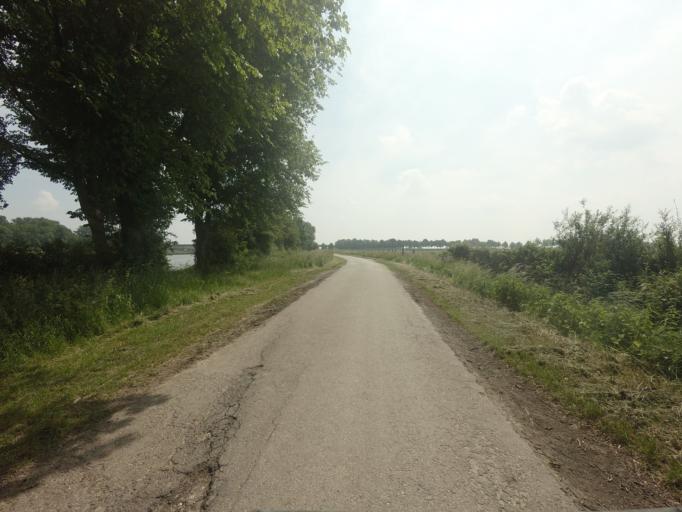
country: NL
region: Gelderland
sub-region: Gemeente Culemborg
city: Culemborg
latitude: 51.9894
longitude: 5.2407
